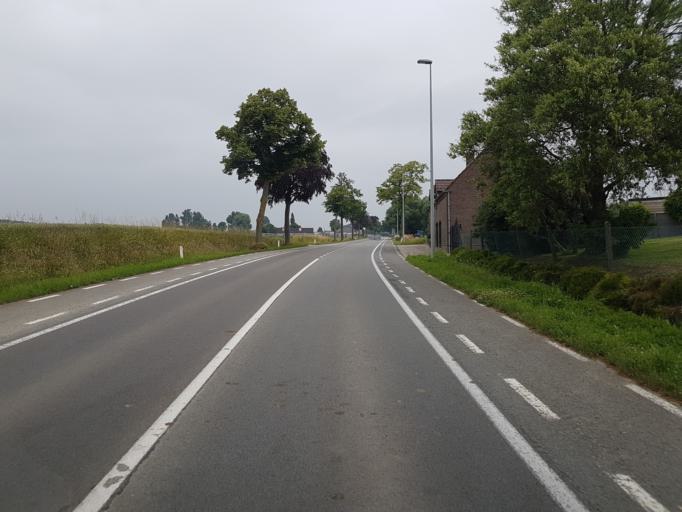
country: BE
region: Flanders
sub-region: Provincie Oost-Vlaanderen
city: Haaltert
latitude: 50.8632
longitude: 3.9593
